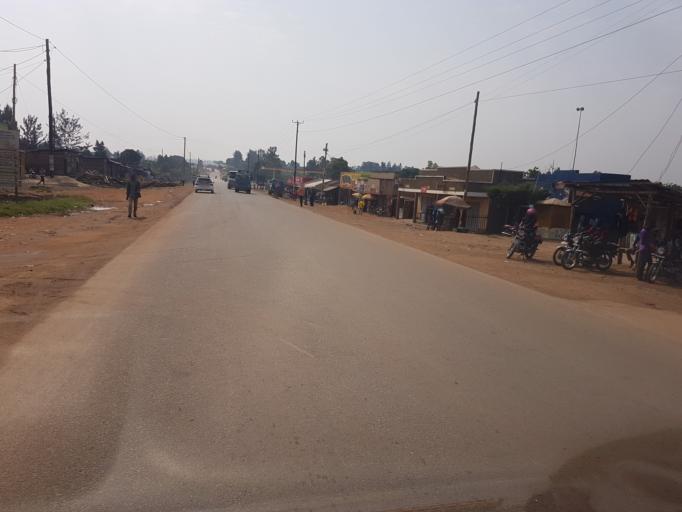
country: UG
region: Western Region
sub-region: Mbarara District
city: Bwizibwera
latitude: -0.6360
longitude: 30.6135
